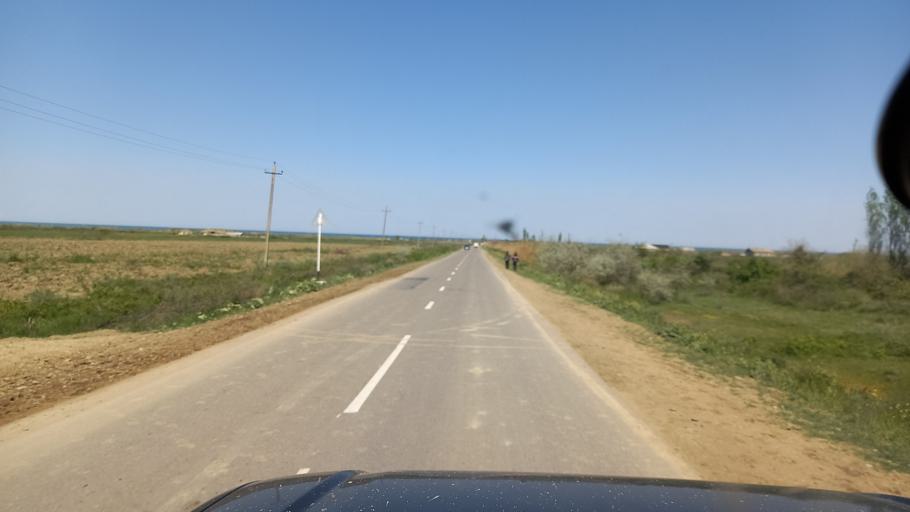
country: RU
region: Dagestan
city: Khazar
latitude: 41.9448
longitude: 48.3458
